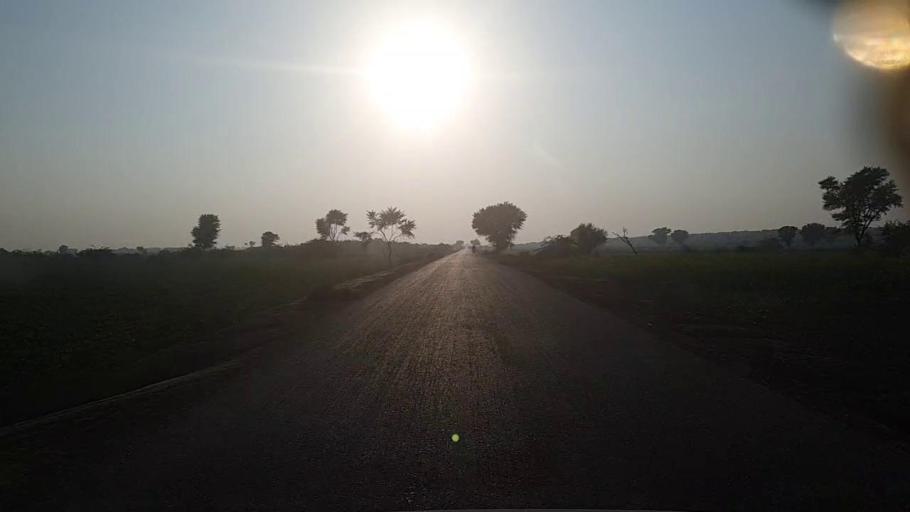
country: PK
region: Sindh
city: Pad Idan
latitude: 26.7127
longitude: 68.3957
